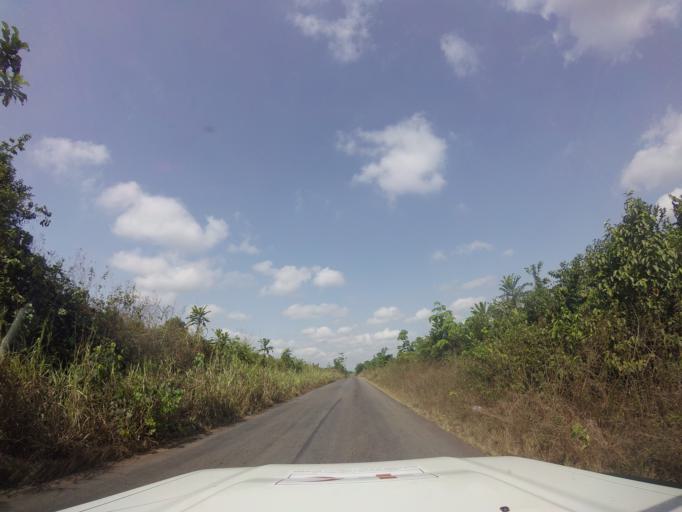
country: LR
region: Bomi
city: Tubmanburg
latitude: 6.7127
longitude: -10.9439
